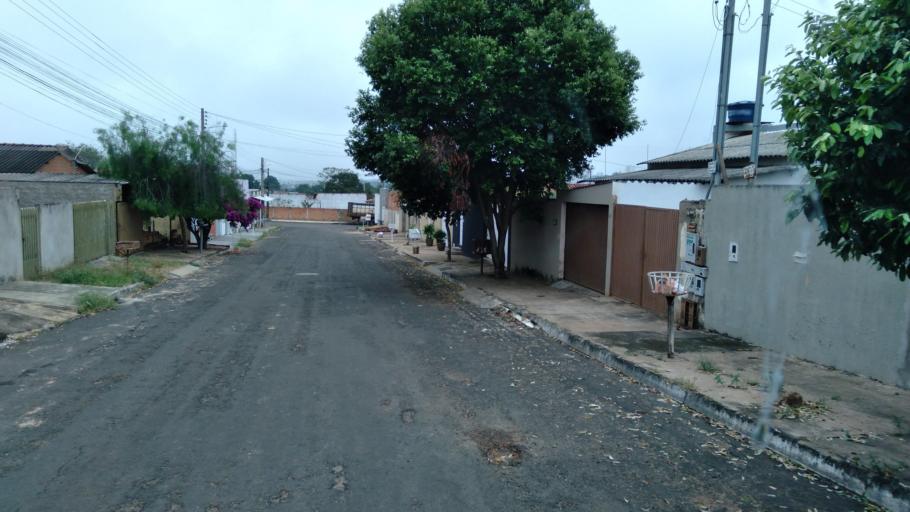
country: BR
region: Goias
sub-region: Mineiros
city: Mineiros
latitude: -17.5746
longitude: -52.5451
